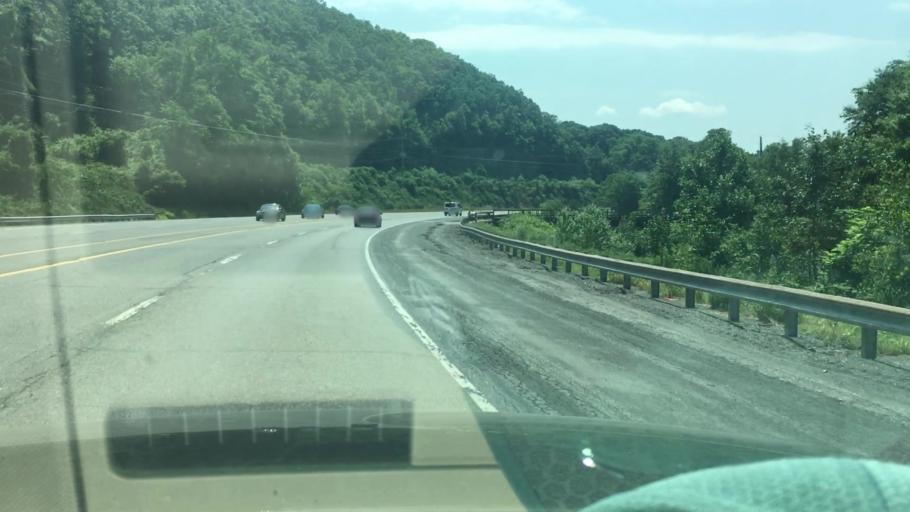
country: US
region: Pennsylvania
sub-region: Schuylkill County
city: Tamaqua
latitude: 40.7738
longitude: -75.9572
